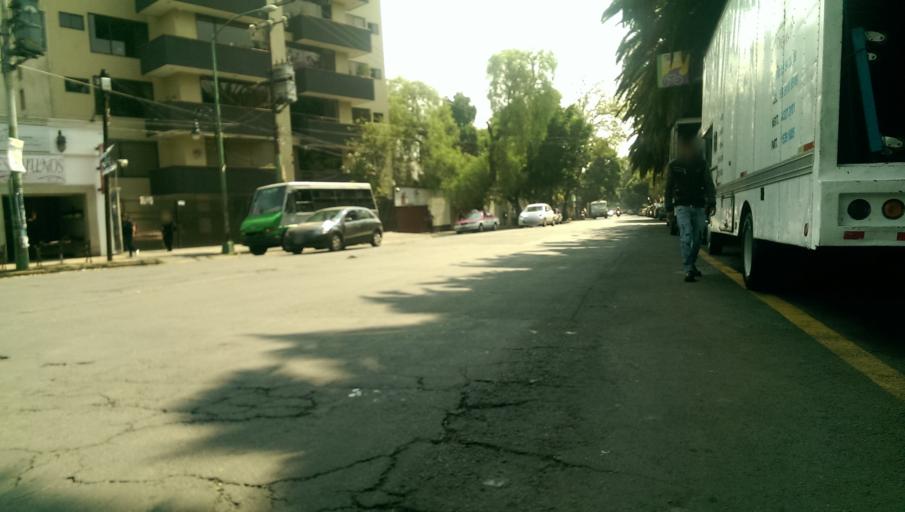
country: MX
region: Mexico City
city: Coyoacan
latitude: 19.3562
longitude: -99.1689
